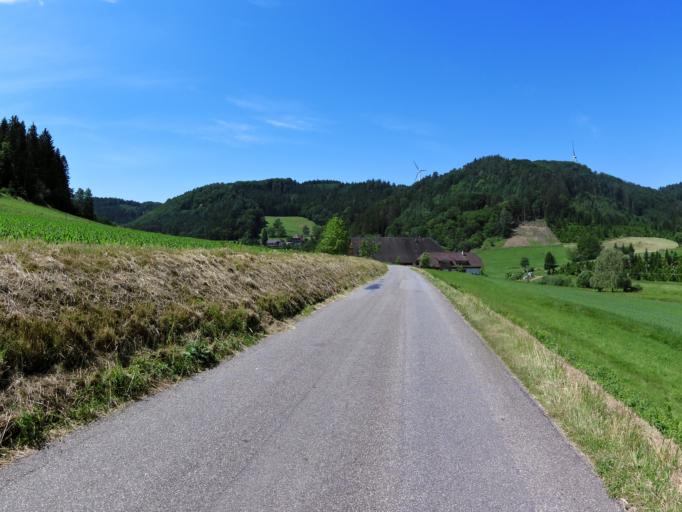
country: DE
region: Baden-Wuerttemberg
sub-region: Freiburg Region
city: Hohberg
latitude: 48.2972
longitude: 7.9197
